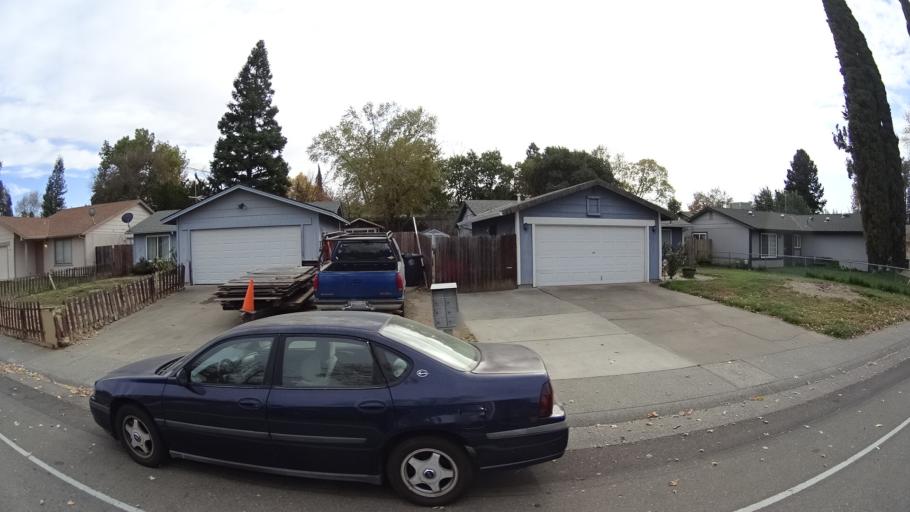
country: US
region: California
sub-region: Sacramento County
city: Citrus Heights
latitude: 38.7059
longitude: -121.2589
